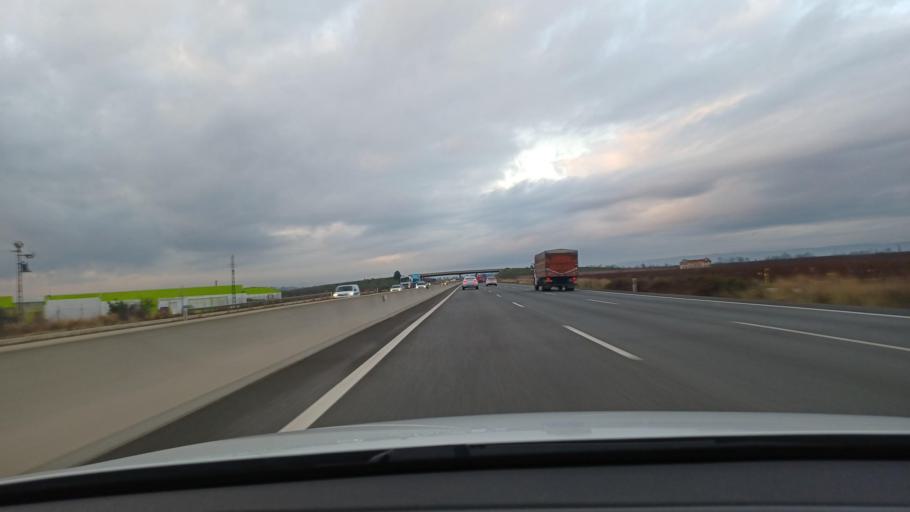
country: ES
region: Valencia
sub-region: Provincia de Valencia
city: L'Alcudia
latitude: 39.2257
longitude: -0.4882
